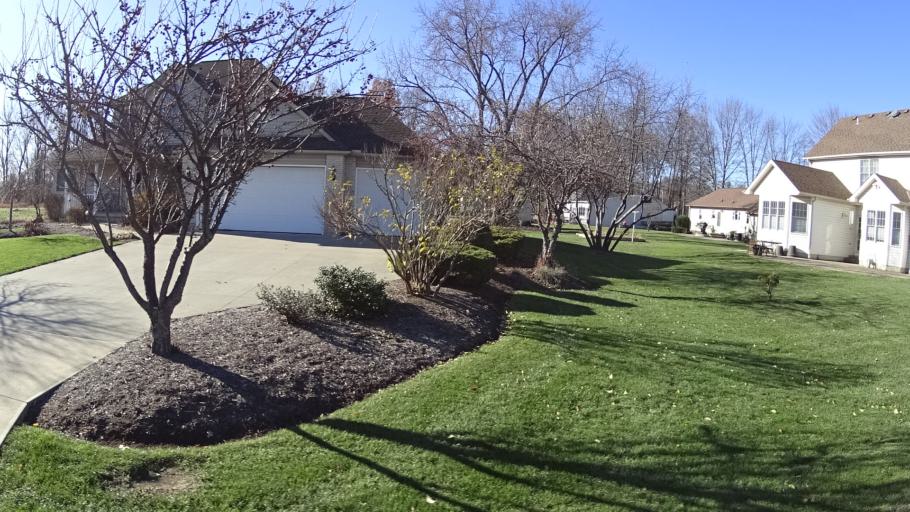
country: US
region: Ohio
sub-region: Lorain County
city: Avon Center
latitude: 41.4415
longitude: -81.9787
